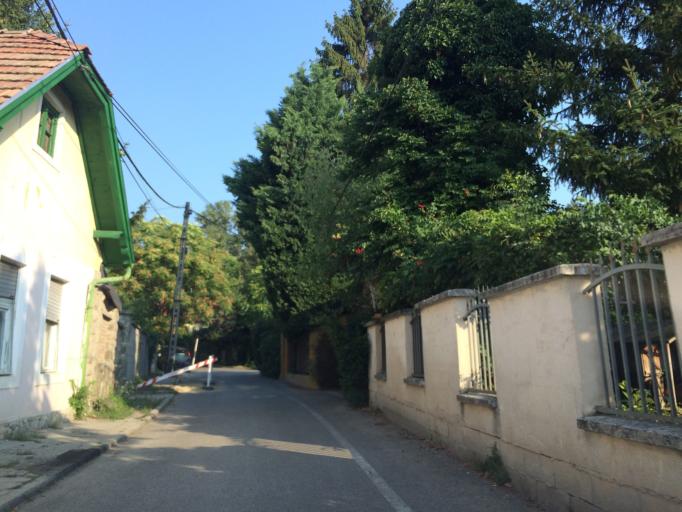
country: HU
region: Pest
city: Szentendre
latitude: 47.6760
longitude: 19.0586
